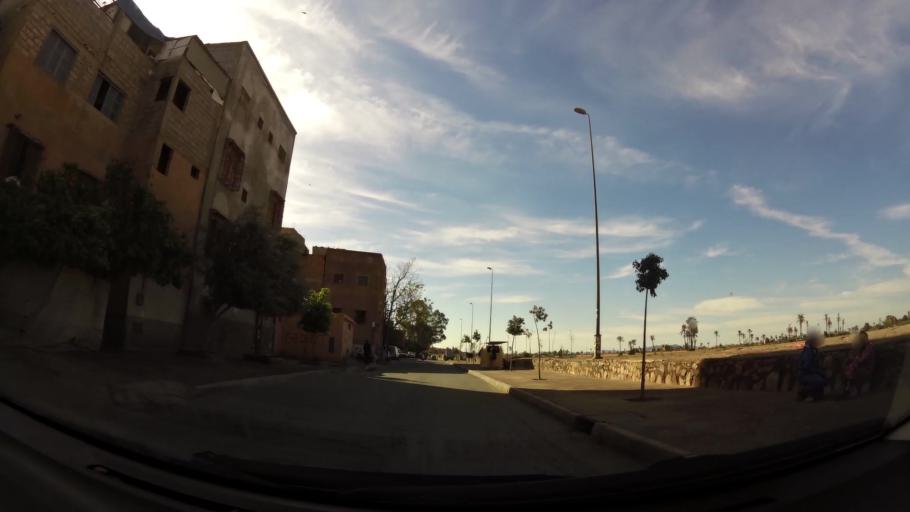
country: MA
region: Marrakech-Tensift-Al Haouz
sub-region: Marrakech
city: Marrakesh
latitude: 31.6139
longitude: -7.9600
